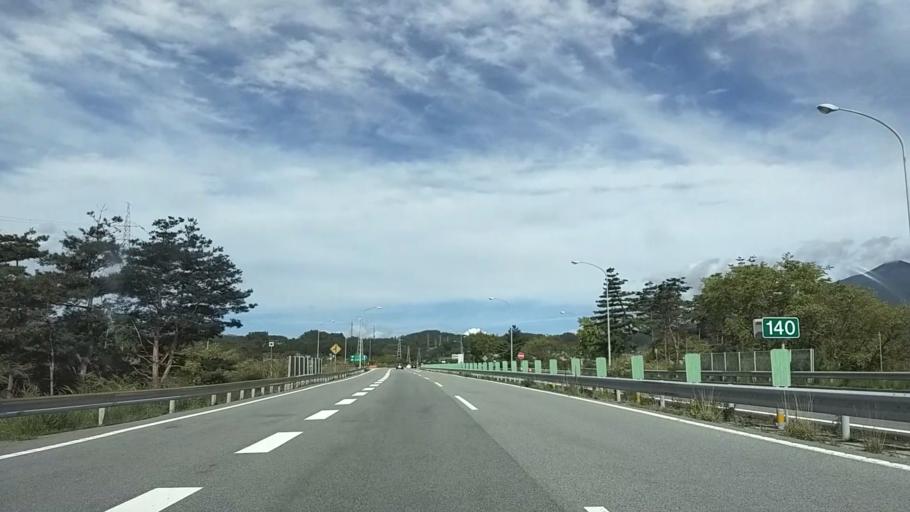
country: JP
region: Yamanashi
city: Nirasaki
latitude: 35.8356
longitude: 138.3895
